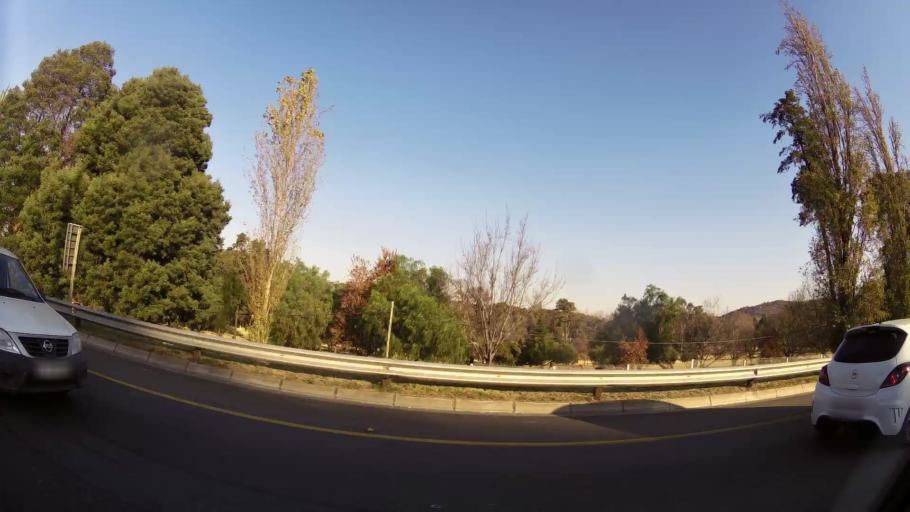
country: ZA
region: Gauteng
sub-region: Ekurhuleni Metropolitan Municipality
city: Germiston
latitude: -26.2615
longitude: 28.1053
